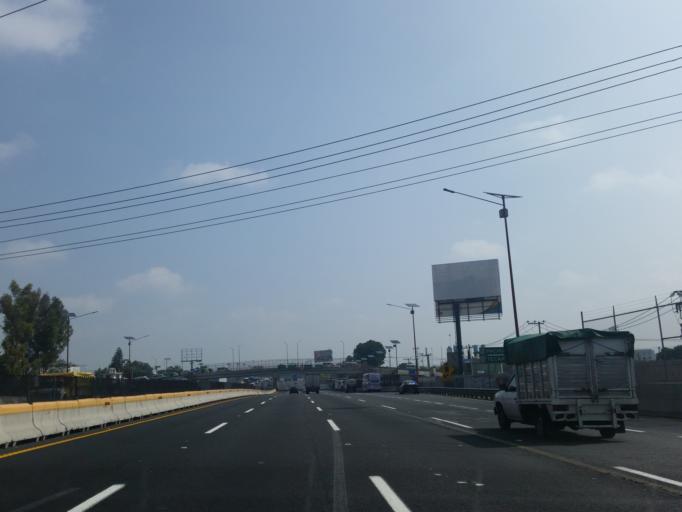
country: MX
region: Mexico
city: Ecatepec
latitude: 19.5940
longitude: -99.0405
